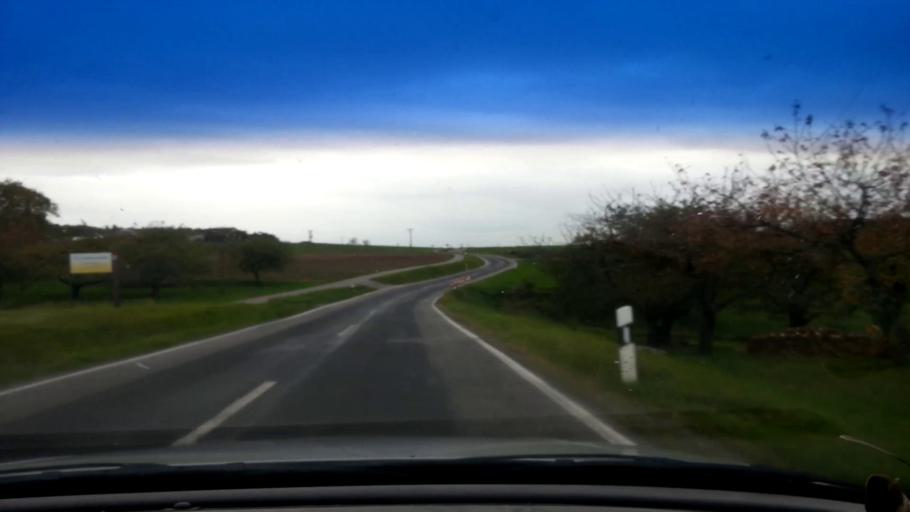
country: DE
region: Bavaria
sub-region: Upper Franconia
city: Priesendorf
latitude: 49.9039
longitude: 10.6642
